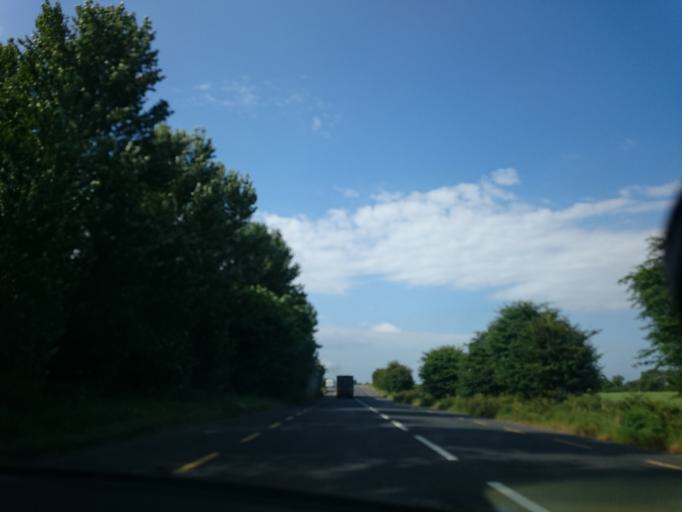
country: IE
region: Leinster
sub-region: Kilkenny
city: Kilkenny
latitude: 52.5996
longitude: -7.2419
